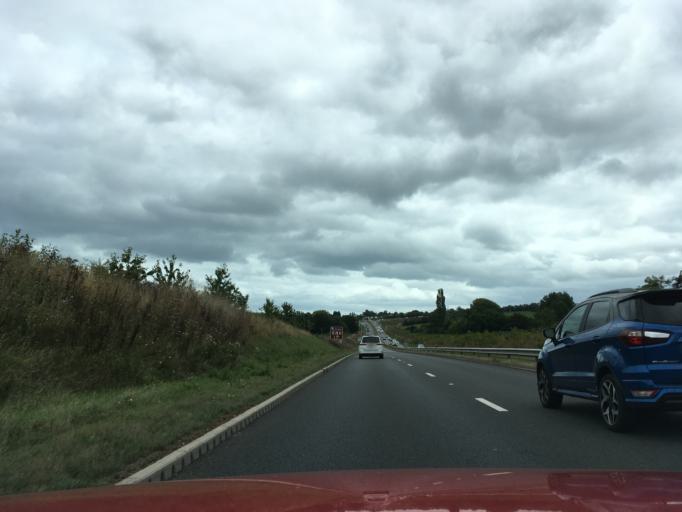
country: GB
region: England
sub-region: Devon
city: Kingskerswell
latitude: 50.4926
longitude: -3.5810
